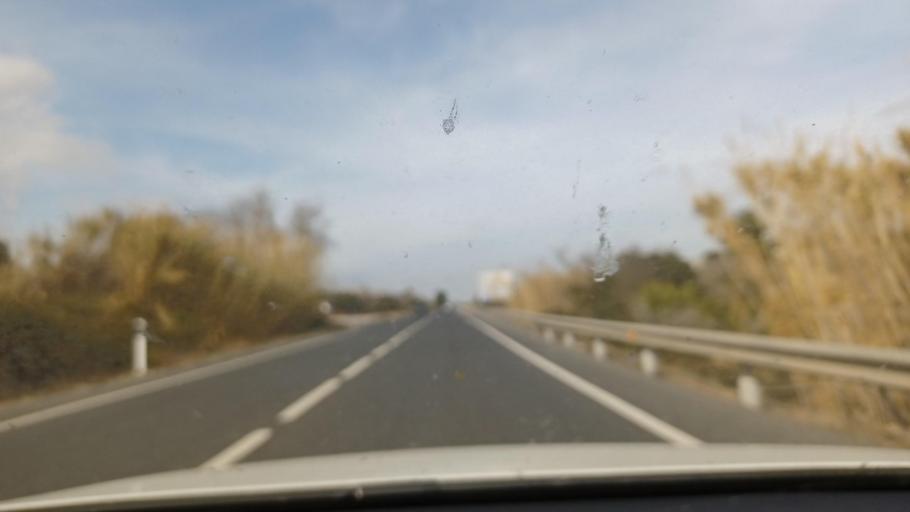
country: ES
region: Catalonia
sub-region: Provincia de Tarragona
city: la Pobla de Mafumet
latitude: 41.1789
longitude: 1.2411
